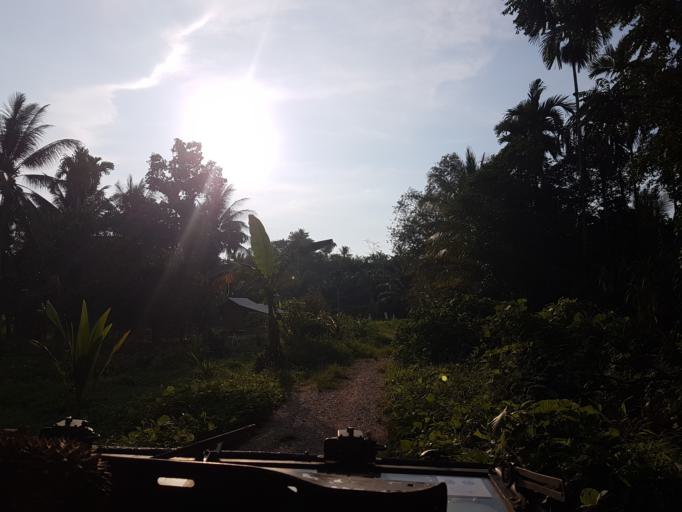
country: TH
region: Pattani
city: Khok Pho
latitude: 6.6655
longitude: 101.0881
